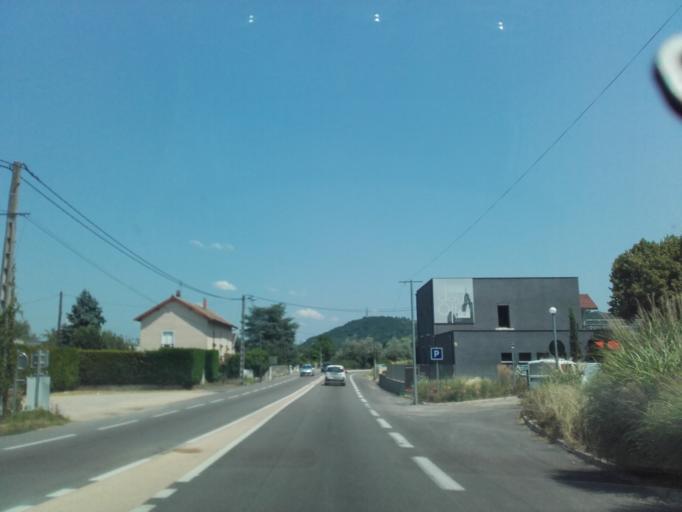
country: FR
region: Rhone-Alpes
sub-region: Departement de l'Isere
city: Saint-Savin
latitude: 45.6238
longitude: 5.2829
